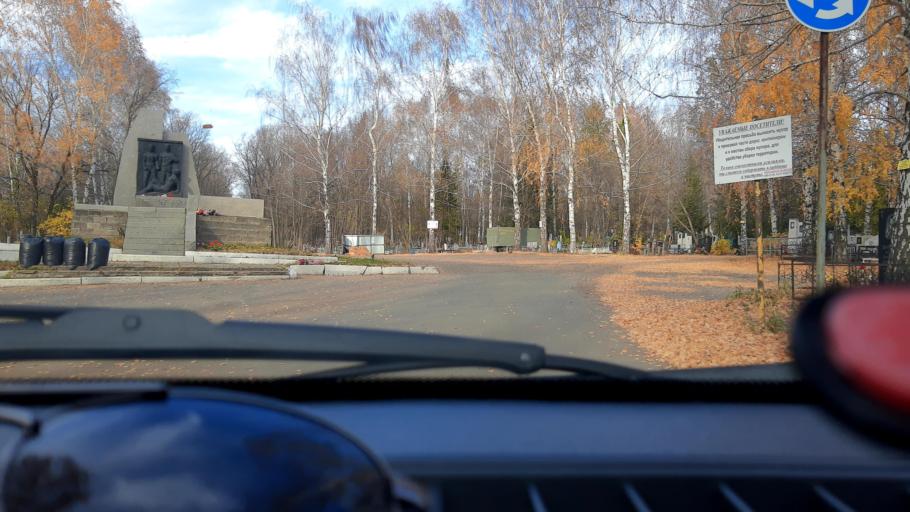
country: RU
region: Bashkortostan
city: Ufa
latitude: 54.8523
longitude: 56.1556
